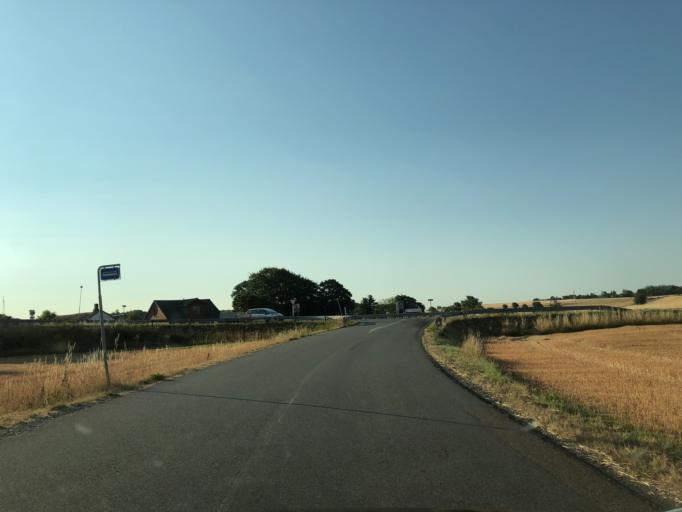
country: DK
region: Central Jutland
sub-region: Skanderborg Kommune
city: Stilling
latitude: 56.0921
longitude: 9.9683
